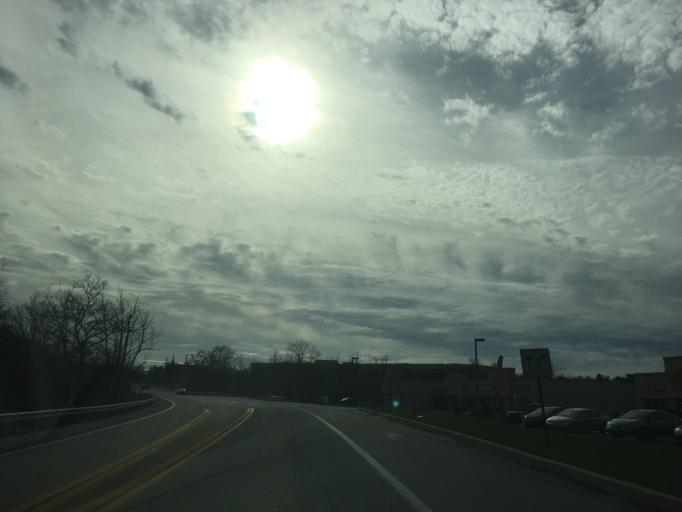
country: US
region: Pennsylvania
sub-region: Dauphin County
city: Colonial Park
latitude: 40.3096
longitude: -76.8238
